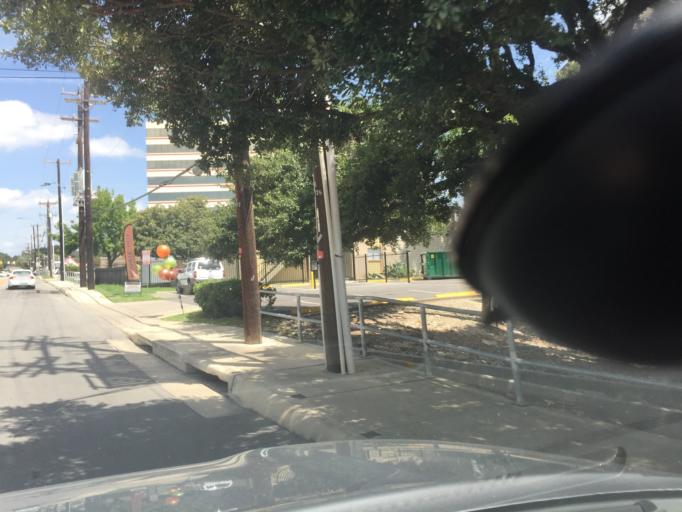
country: US
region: Texas
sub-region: Bexar County
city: Castle Hills
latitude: 29.5298
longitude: -98.4945
